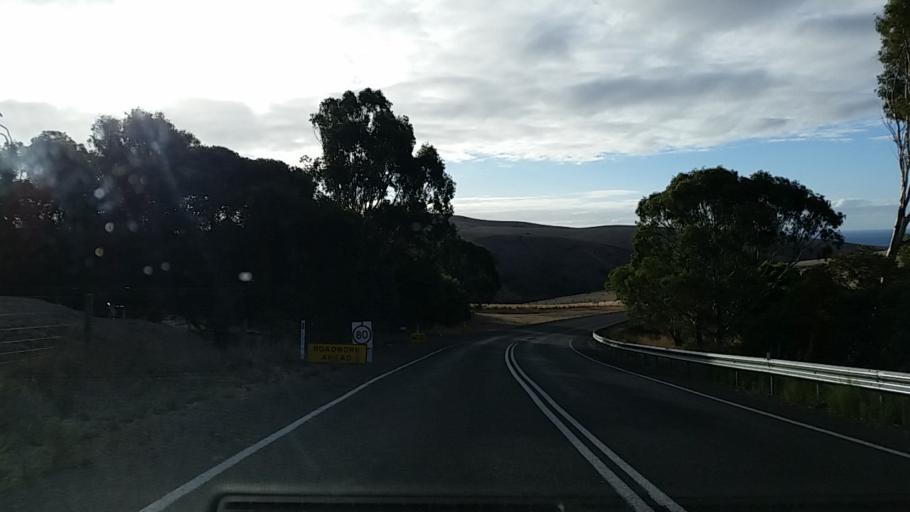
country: AU
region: South Australia
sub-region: Yankalilla
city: Normanville
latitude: -35.5533
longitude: 138.1965
